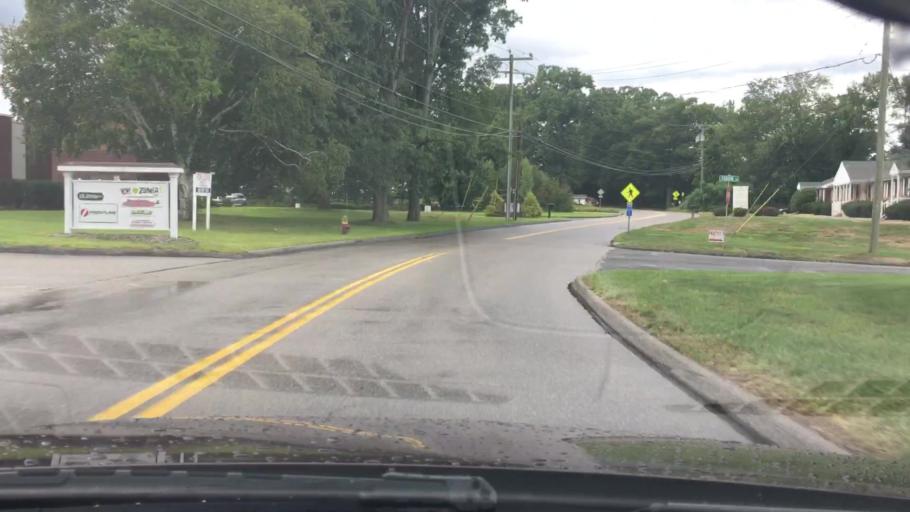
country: US
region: Connecticut
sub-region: Hartford County
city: Glastonbury Center
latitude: 41.7124
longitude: -72.5848
